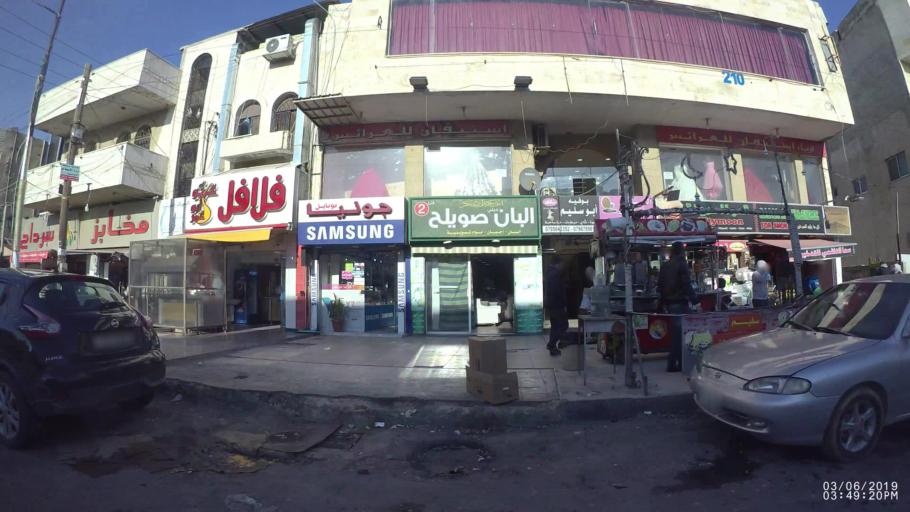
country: JO
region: Amman
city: Amman
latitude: 31.9729
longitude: 35.9506
